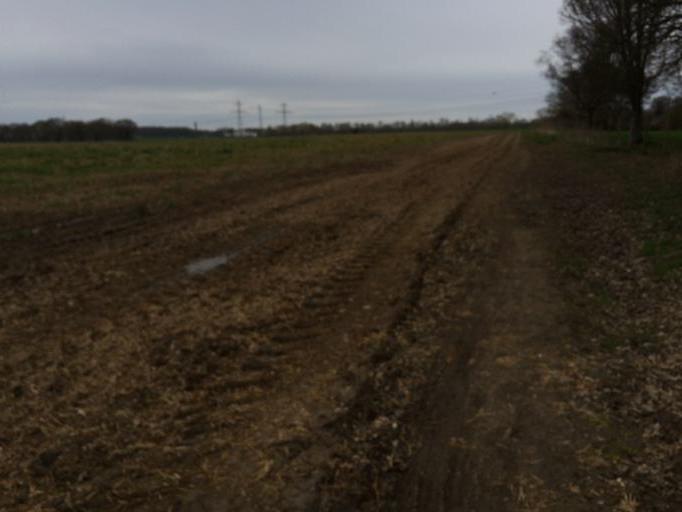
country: FR
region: Ile-de-France
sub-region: Departement des Yvelines
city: Les Loges-en-Josas
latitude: 48.7466
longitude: 2.1454
